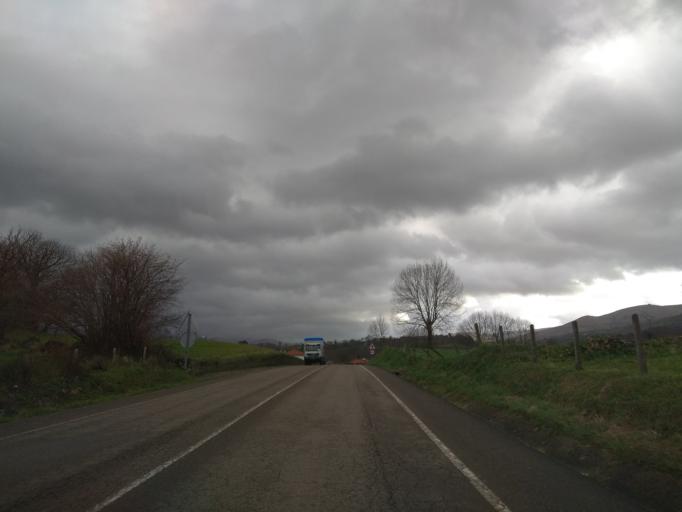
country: ES
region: Cantabria
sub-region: Provincia de Cantabria
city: Saro
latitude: 43.2426
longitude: -3.8455
